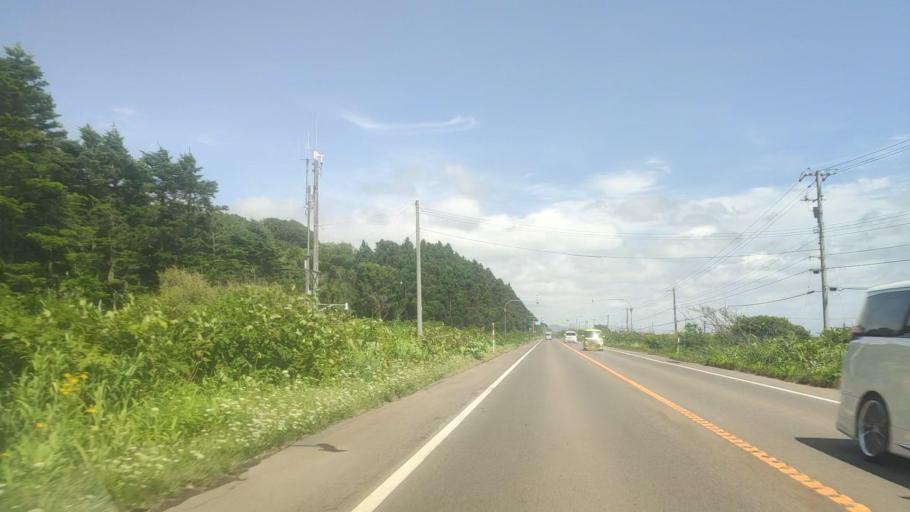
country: JP
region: Hokkaido
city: Niseko Town
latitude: 42.3370
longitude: 140.2797
